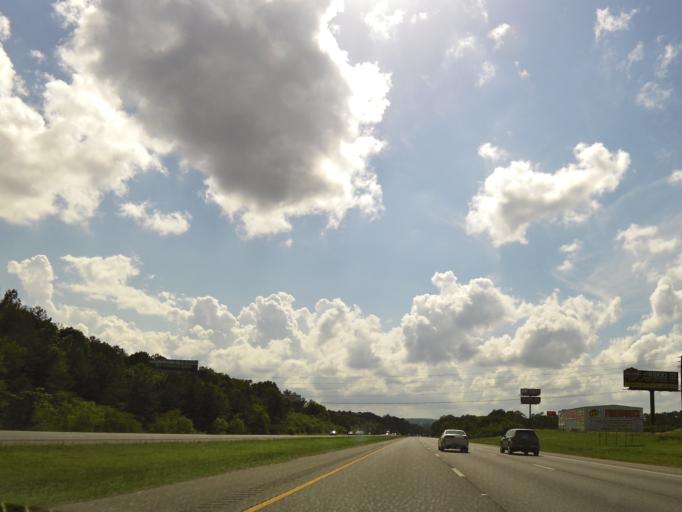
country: US
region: Alabama
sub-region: Jefferson County
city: Leeds
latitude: 33.5435
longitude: -86.6032
